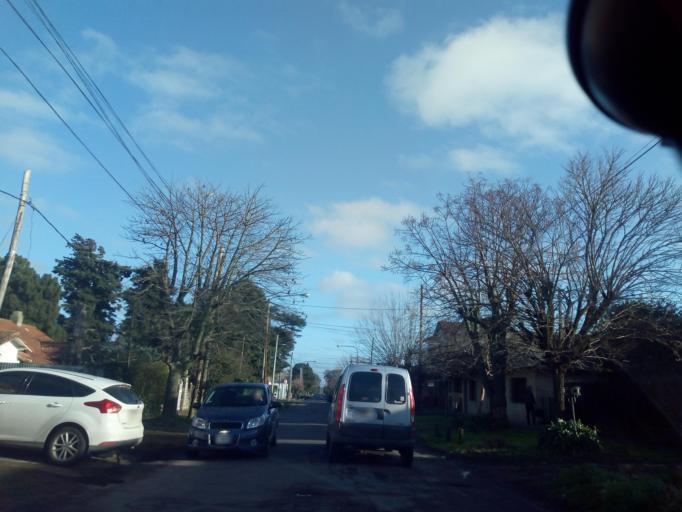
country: AR
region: Buenos Aires
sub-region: Partido de La Plata
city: La Plata
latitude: -34.9444
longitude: -57.9844
